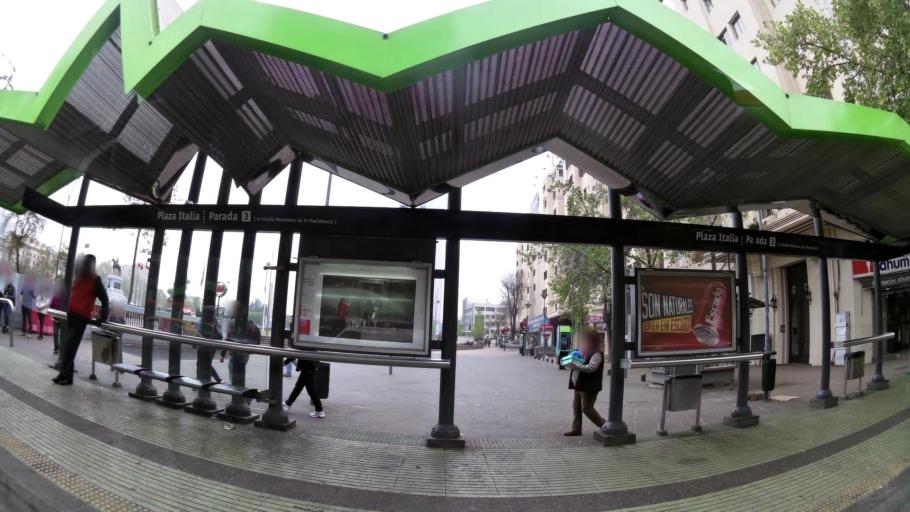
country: CL
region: Santiago Metropolitan
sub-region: Provincia de Santiago
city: Santiago
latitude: -33.4377
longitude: -70.6350
